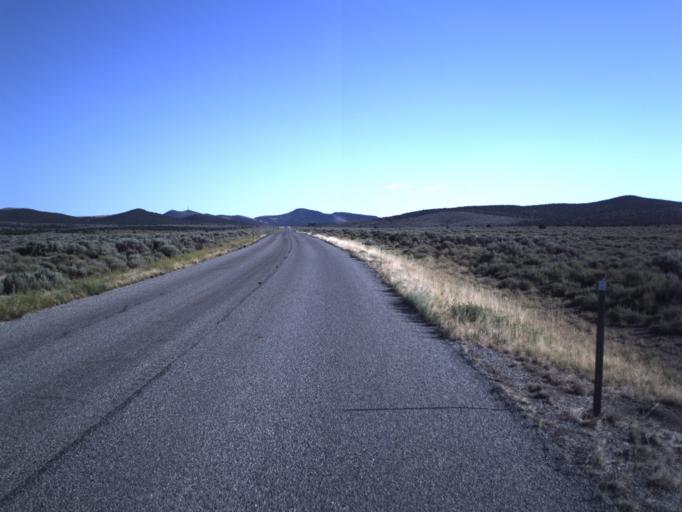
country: US
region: Utah
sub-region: Iron County
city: Enoch
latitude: 38.0032
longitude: -112.9978
